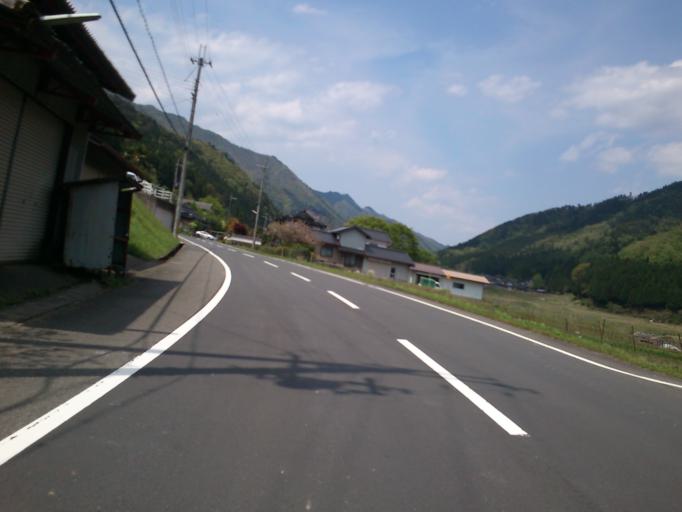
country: JP
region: Kyoto
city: Fukuchiyama
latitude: 35.3583
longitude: 134.9401
